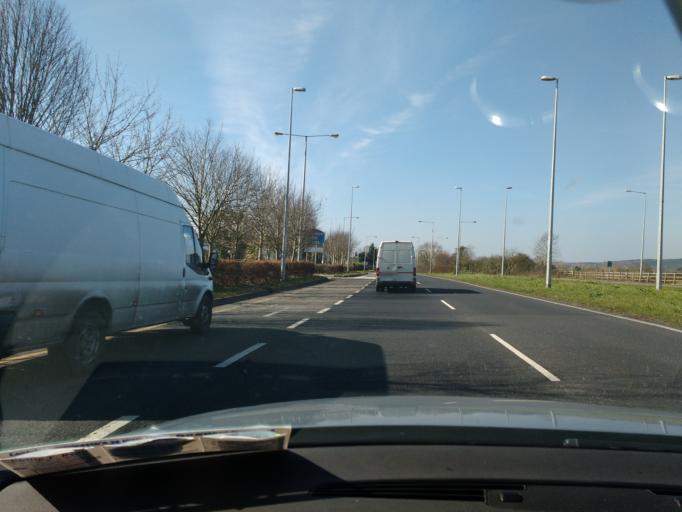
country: IE
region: Munster
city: Moyross
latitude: 52.6796
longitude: -8.6980
